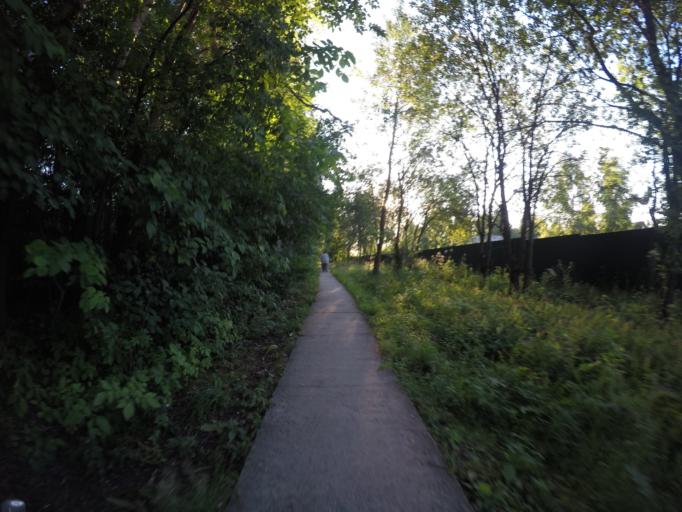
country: RU
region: Moskovskaya
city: Rechitsy
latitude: 55.6044
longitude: 38.5020
